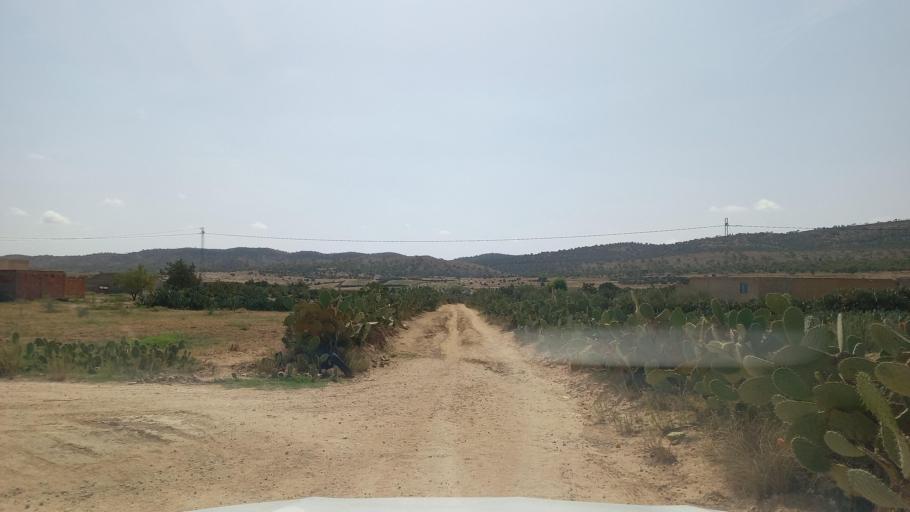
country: TN
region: Al Qasrayn
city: Sbiba
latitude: 35.3874
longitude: 8.9564
